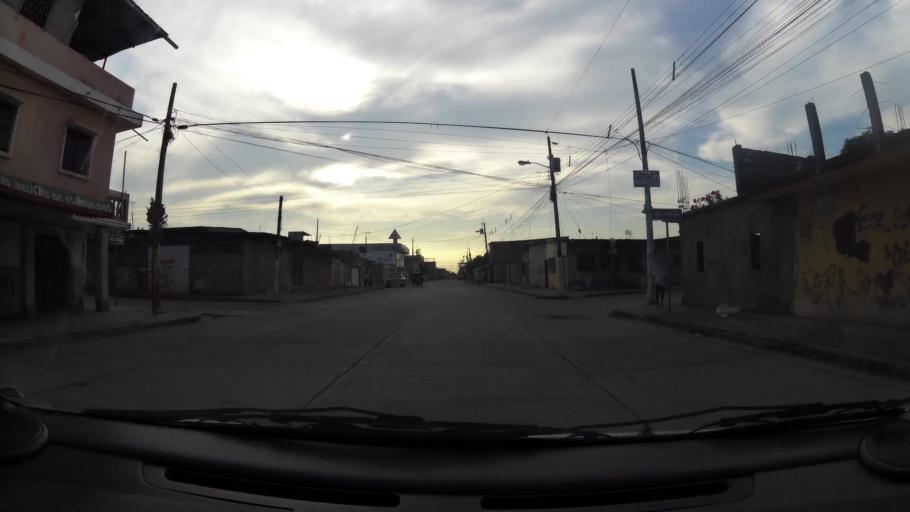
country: EC
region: Guayas
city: Eloy Alfaro
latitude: -2.0916
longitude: -79.9071
